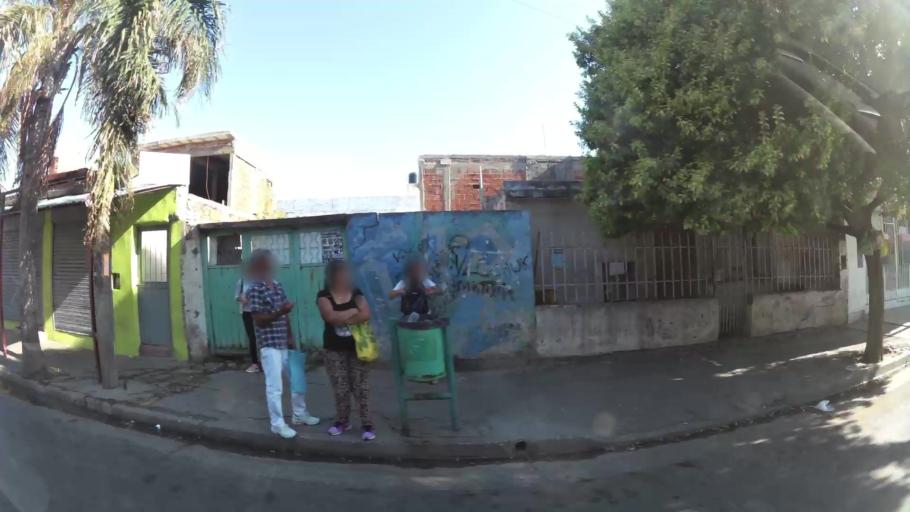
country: AR
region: Cordoba
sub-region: Departamento de Capital
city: Cordoba
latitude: -31.4755
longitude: -64.2211
